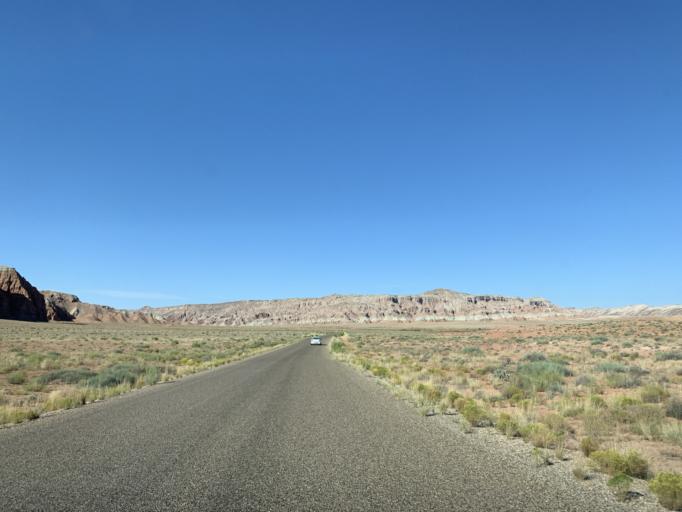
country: US
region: Utah
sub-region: Emery County
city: Ferron
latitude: 38.5794
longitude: -110.7314
